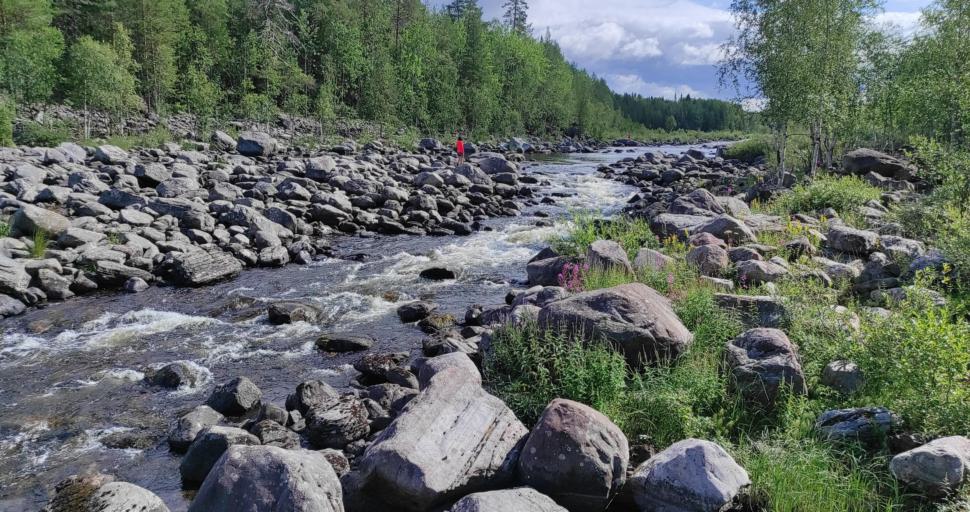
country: RU
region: Murmansk
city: Poyakonda
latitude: 66.6762
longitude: 32.8620
